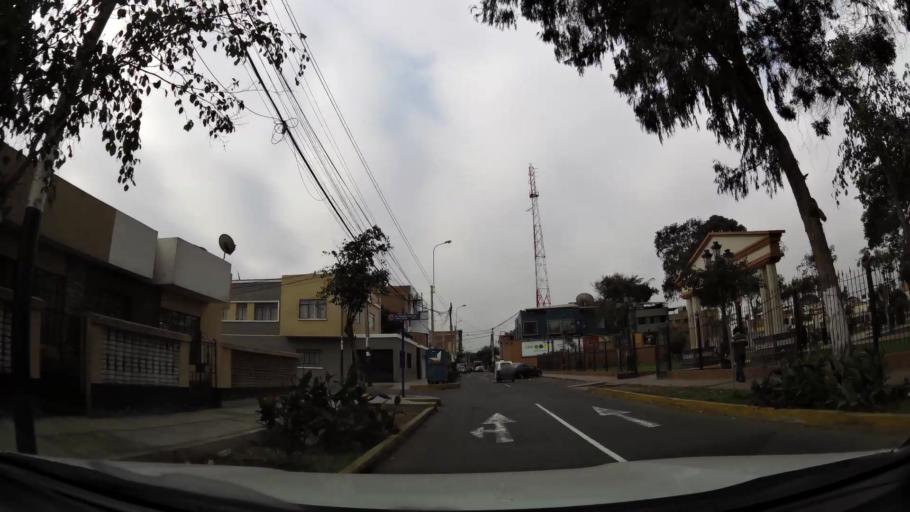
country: PE
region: Lima
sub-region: Lima
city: Surco
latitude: -12.1702
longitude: -77.0213
